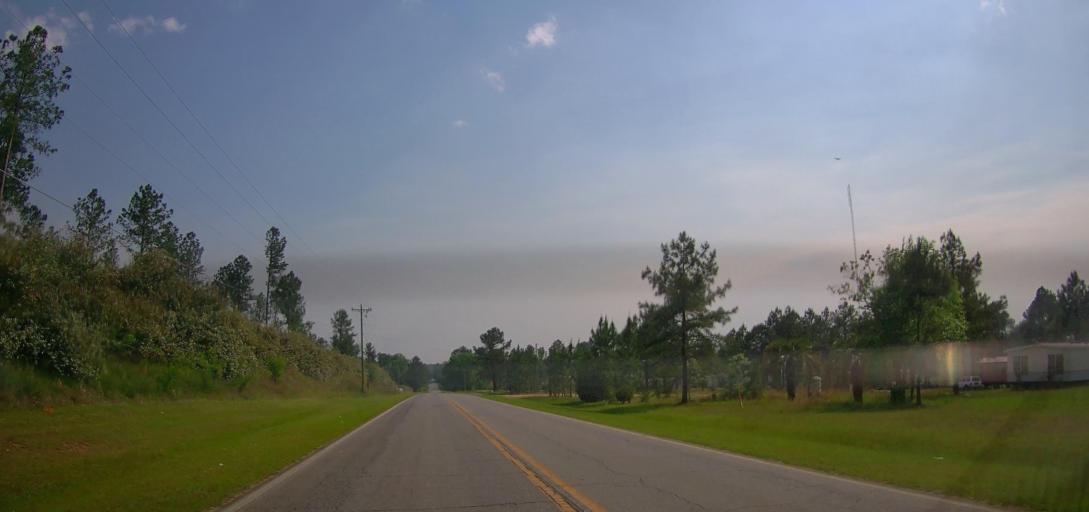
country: US
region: Georgia
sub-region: Laurens County
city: East Dublin
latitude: 32.5776
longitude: -82.8643
